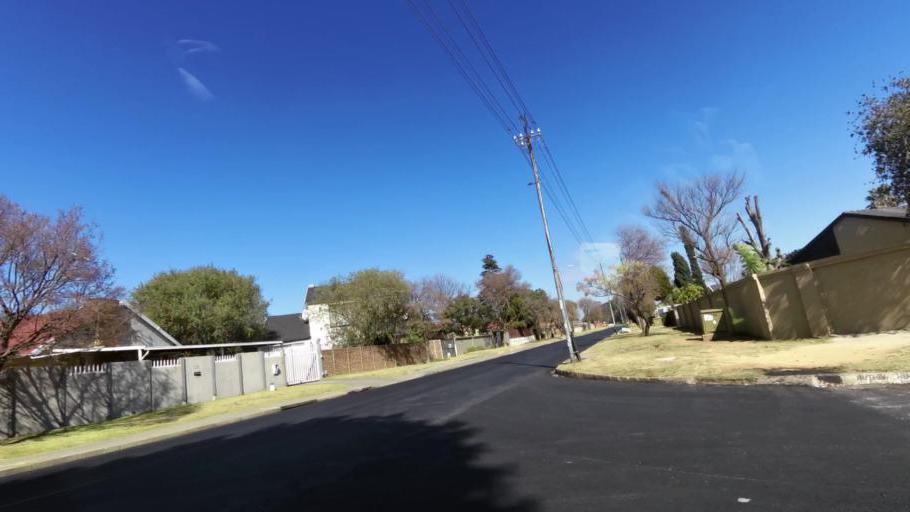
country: ZA
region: Gauteng
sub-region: City of Johannesburg Metropolitan Municipality
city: Johannesburg
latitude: -26.2454
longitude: 28.0012
